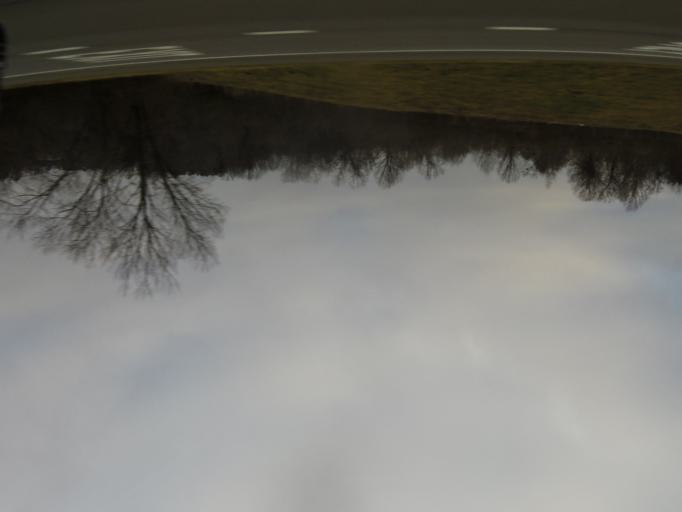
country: US
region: Alabama
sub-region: Jefferson County
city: Fultondale
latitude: 33.5978
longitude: -86.8069
